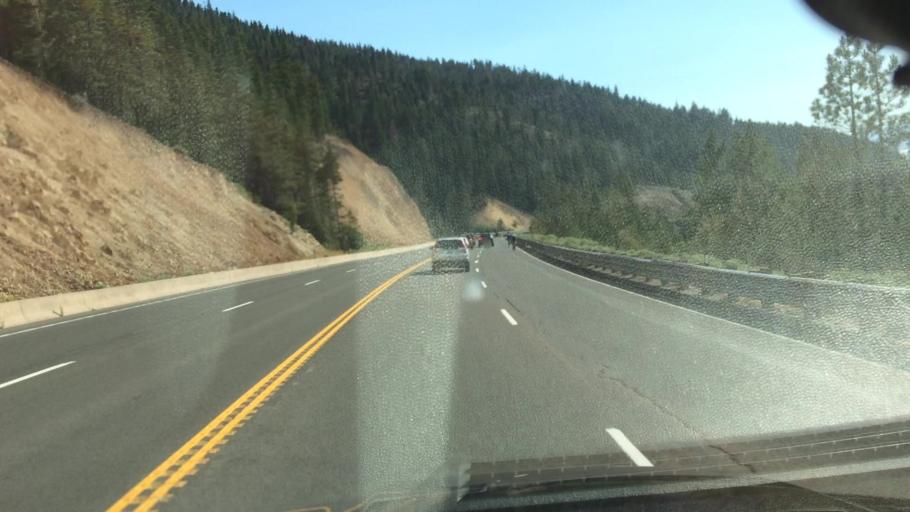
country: US
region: Nevada
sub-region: Douglas County
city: Kingsbury
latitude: 39.0872
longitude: -119.9140
